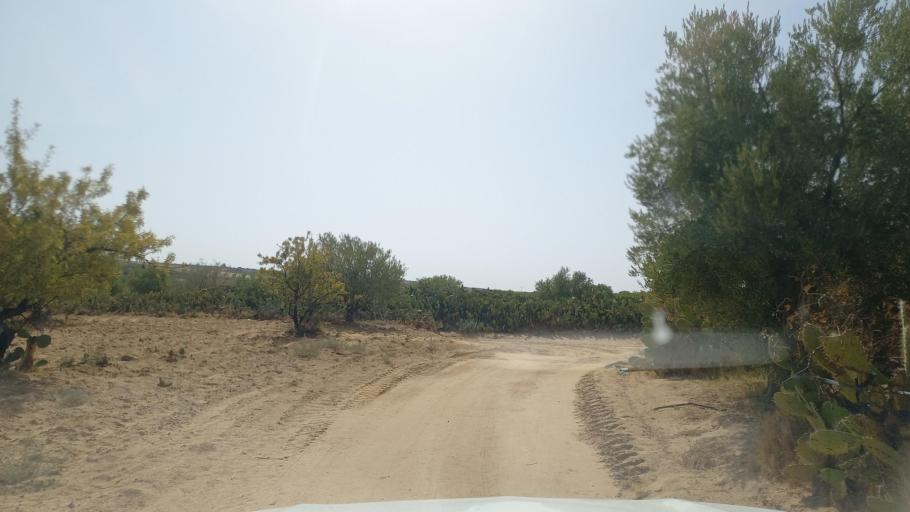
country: TN
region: Al Qasrayn
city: Kasserine
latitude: 35.2428
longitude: 9.0481
